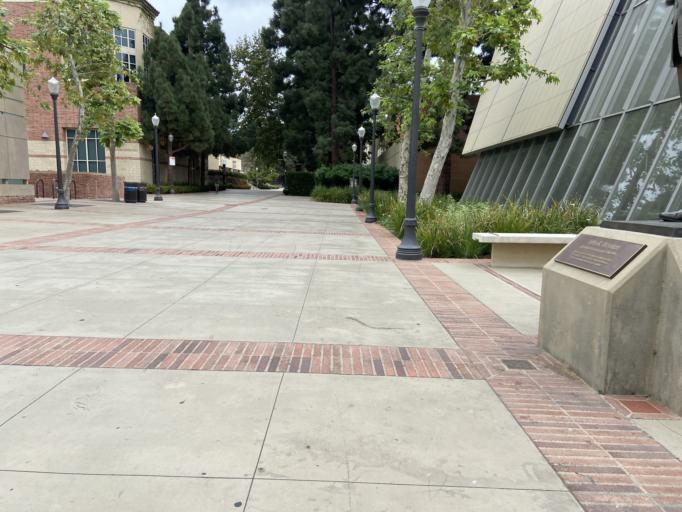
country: US
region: California
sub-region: Los Angeles County
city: Westwood, Los Angeles
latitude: 34.0709
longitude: -118.4465
